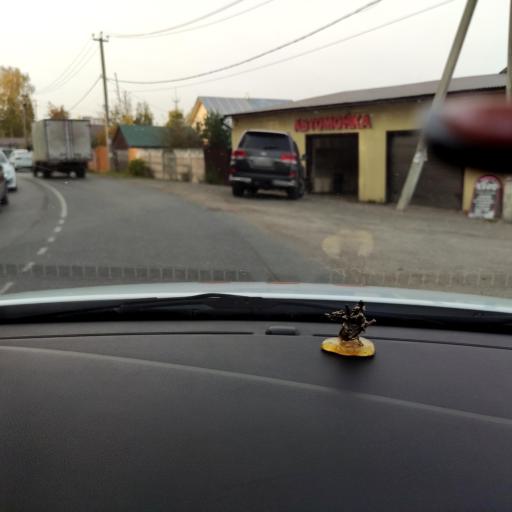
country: RU
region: Tatarstan
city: Vysokaya Gora
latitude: 55.9272
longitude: 49.3032
